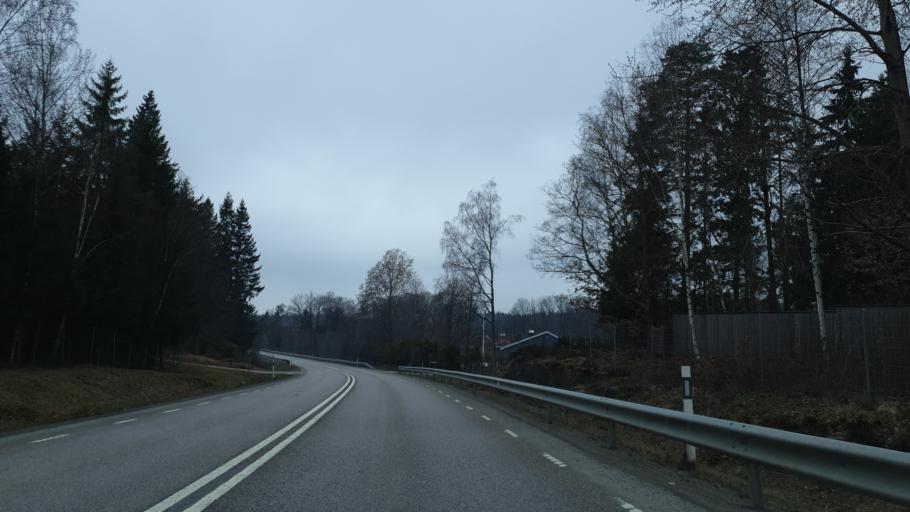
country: SE
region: Vaestra Goetaland
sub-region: Harryda Kommun
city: Hindas
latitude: 57.6530
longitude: 12.3948
